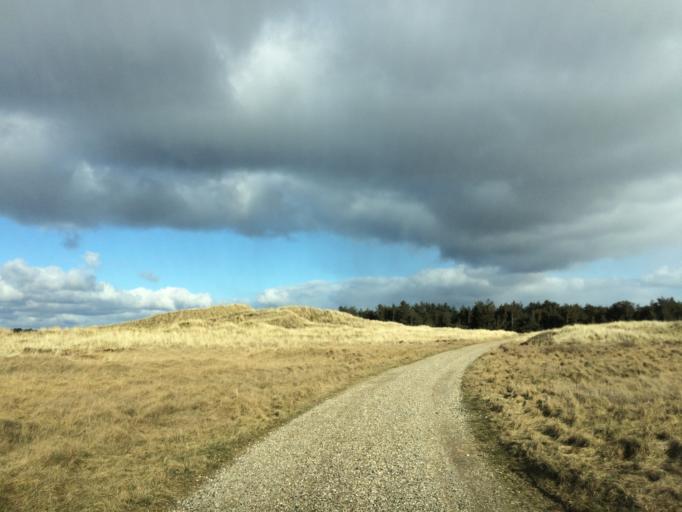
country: DK
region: Central Jutland
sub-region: Holstebro Kommune
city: Ulfborg
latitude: 56.2806
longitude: 8.1371
